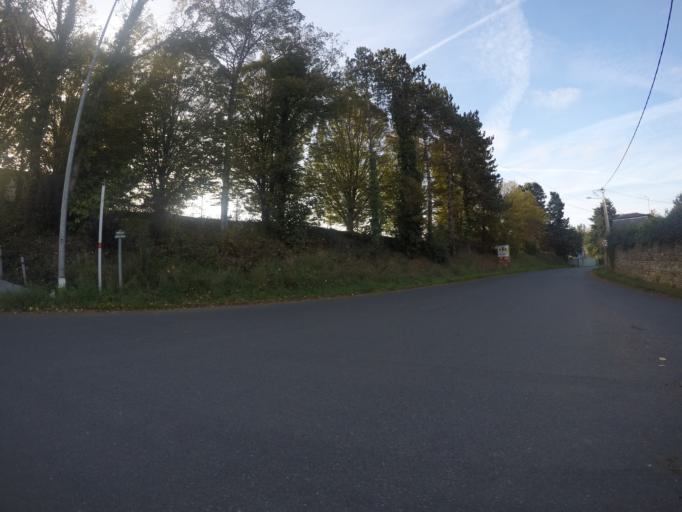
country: FR
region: Brittany
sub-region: Departement des Cotes-d'Armor
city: Guingamp
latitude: 48.5515
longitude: -3.1580
